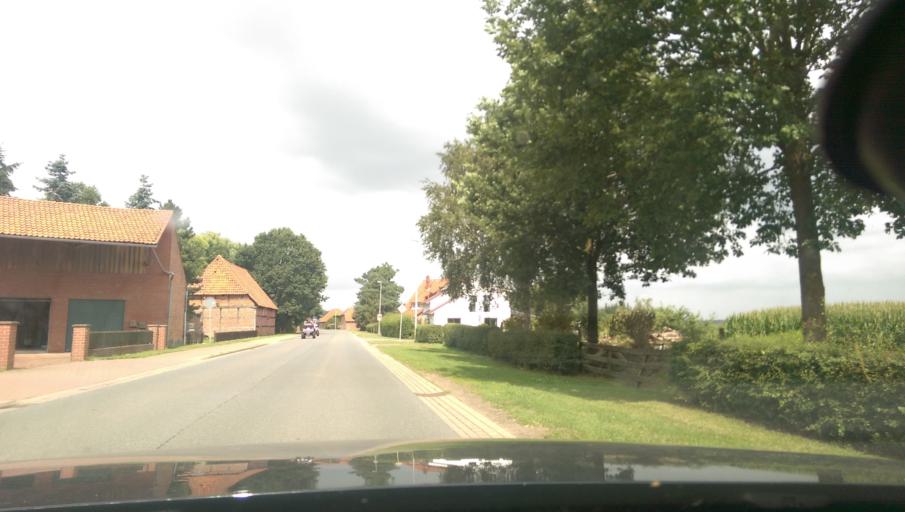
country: DE
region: Lower Saxony
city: Steimbke
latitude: 52.6857
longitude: 9.4816
